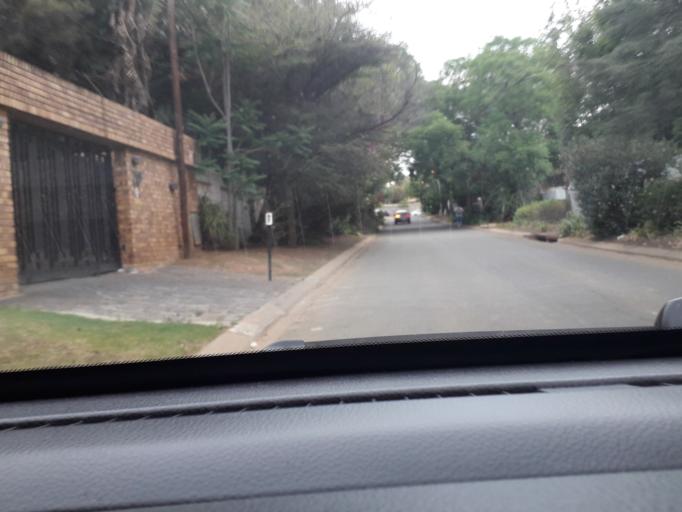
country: ZA
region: Gauteng
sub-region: City of Johannesburg Metropolitan Municipality
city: Midrand
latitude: -26.0530
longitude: 28.0572
